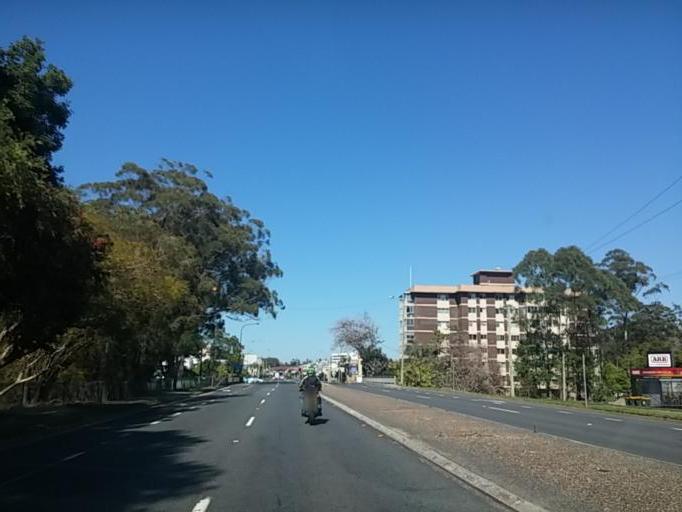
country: AU
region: New South Wales
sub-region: Coffs Harbour
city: Coffs Harbour
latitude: -30.2930
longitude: 153.1172
